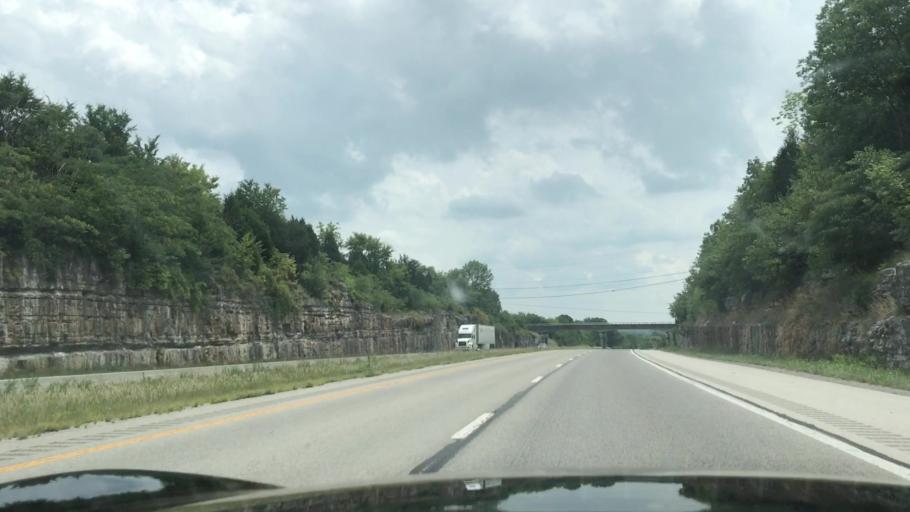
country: US
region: Kentucky
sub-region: Warren County
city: Bowling Green
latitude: 37.0044
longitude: -86.5076
